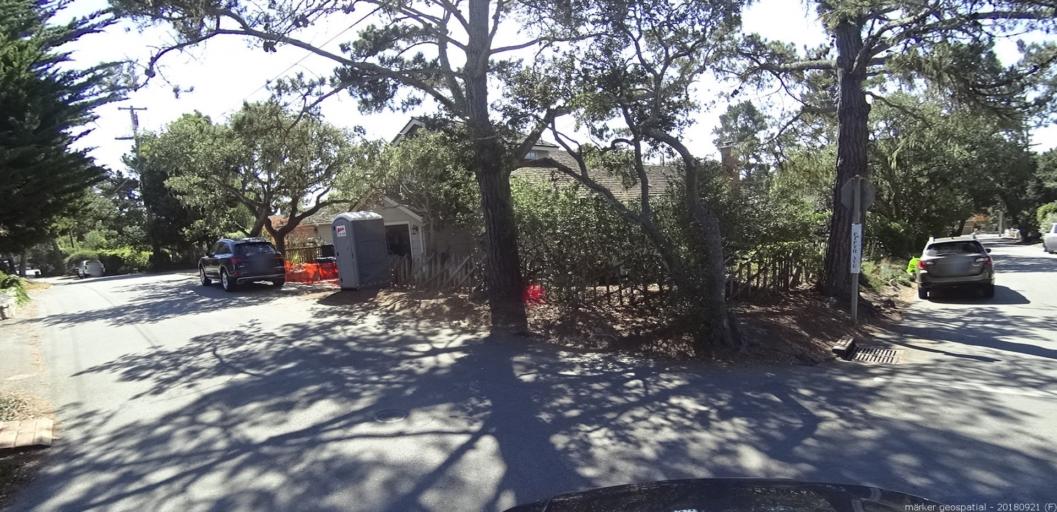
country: US
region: California
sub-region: Monterey County
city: Carmel-by-the-Sea
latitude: 36.5569
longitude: -121.9149
